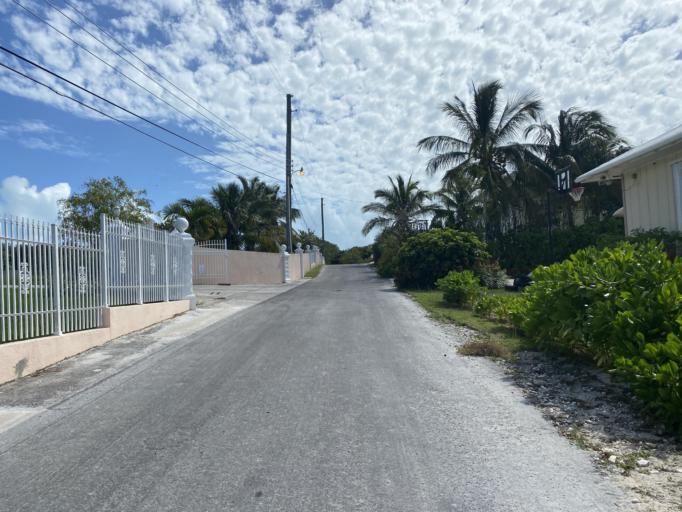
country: BS
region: Spanish Wells
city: Spanish Wells
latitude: 25.5455
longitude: -76.7758
